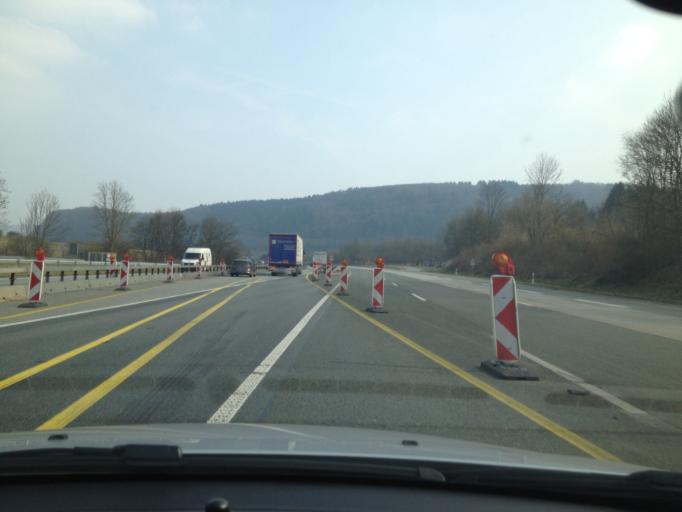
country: DE
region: Hesse
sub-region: Regierungsbezirk Giessen
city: Haiger
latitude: 50.7459
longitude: 8.2317
